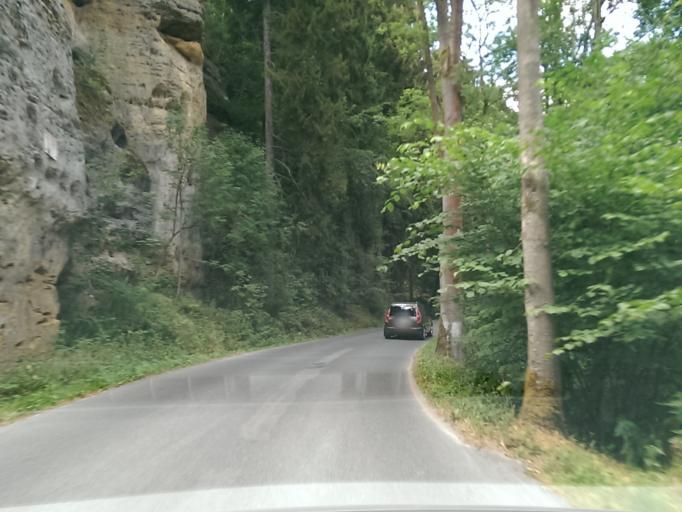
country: CZ
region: Central Bohemia
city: Mseno
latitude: 50.4187
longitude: 14.5759
